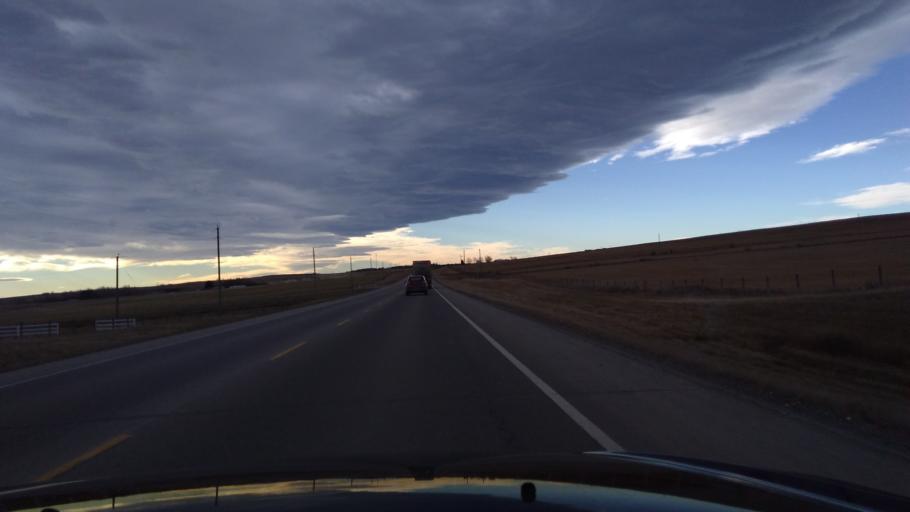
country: CA
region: Alberta
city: Cochrane
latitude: 51.1355
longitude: -114.4669
